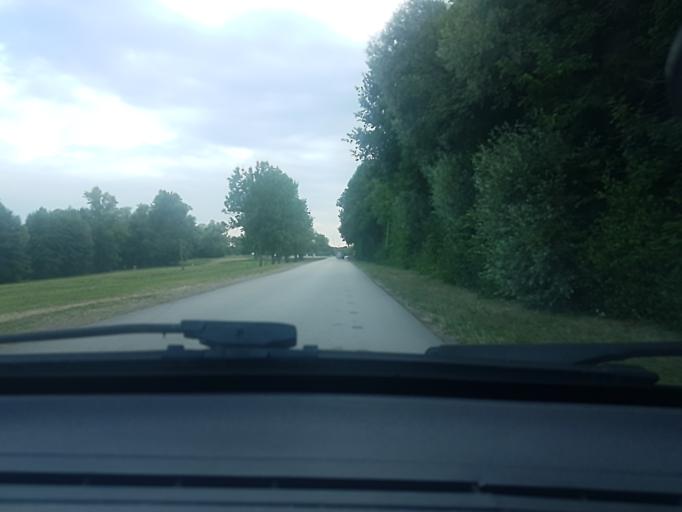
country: FR
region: Bourgogne
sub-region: Departement de Saone-et-Loire
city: Sennecey-le-Grand
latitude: 46.6692
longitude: 4.8241
